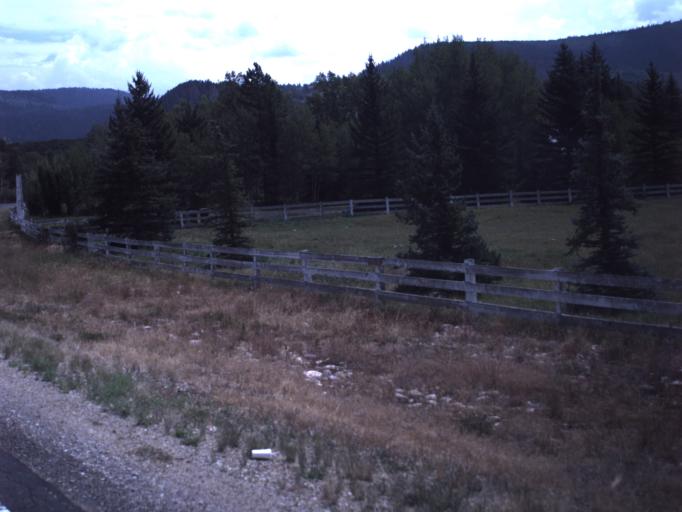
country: US
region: Utah
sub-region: Summit County
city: Francis
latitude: 40.5585
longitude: -111.1411
